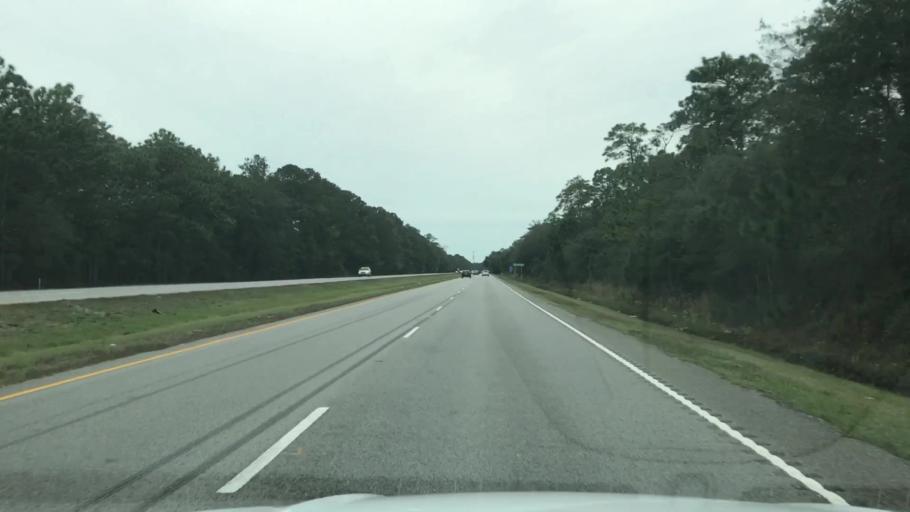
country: US
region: South Carolina
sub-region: Georgetown County
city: Georgetown
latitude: 33.3816
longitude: -79.2085
